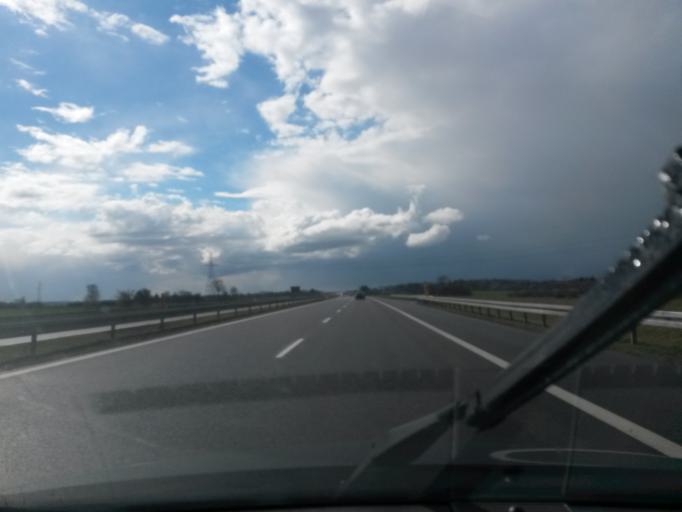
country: PL
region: Greater Poland Voivodeship
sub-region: Powiat wrzesinski
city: Wrzesnia
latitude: 52.3180
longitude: 17.5100
